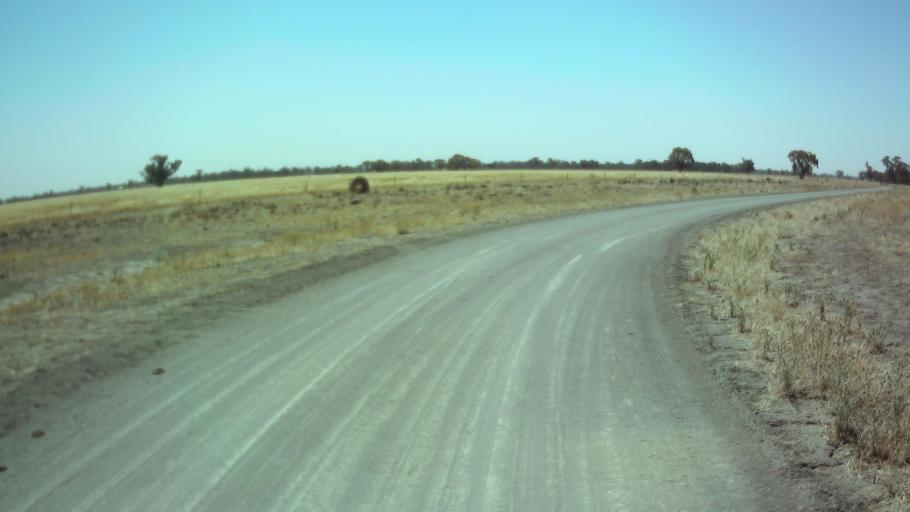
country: AU
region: New South Wales
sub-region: Weddin
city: Grenfell
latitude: -33.9946
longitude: 147.8653
